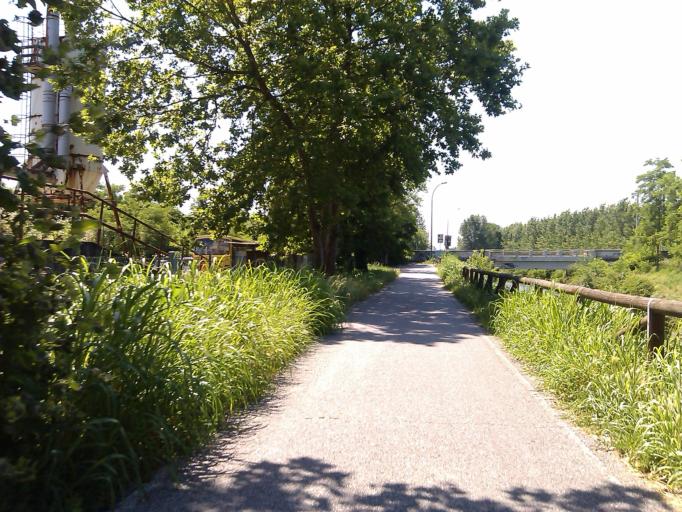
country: IT
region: Veneto
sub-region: Provincia di Treviso
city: Castelfranco Veneto
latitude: 45.6663
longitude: 11.9222
